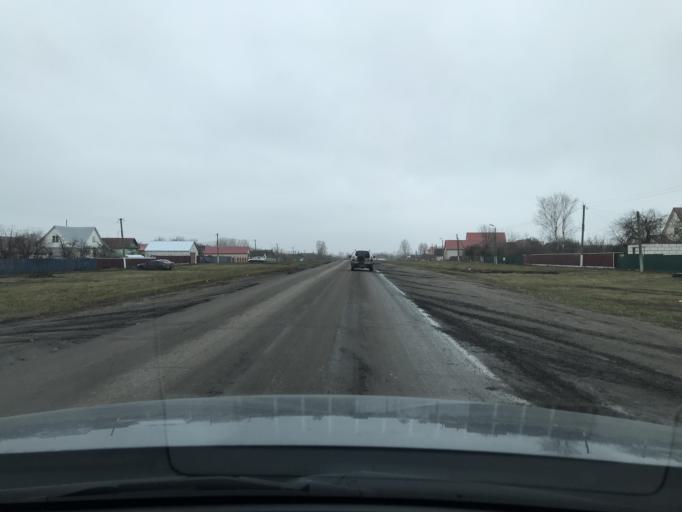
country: RU
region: Penza
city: Zemetchino
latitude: 53.5053
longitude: 42.6348
